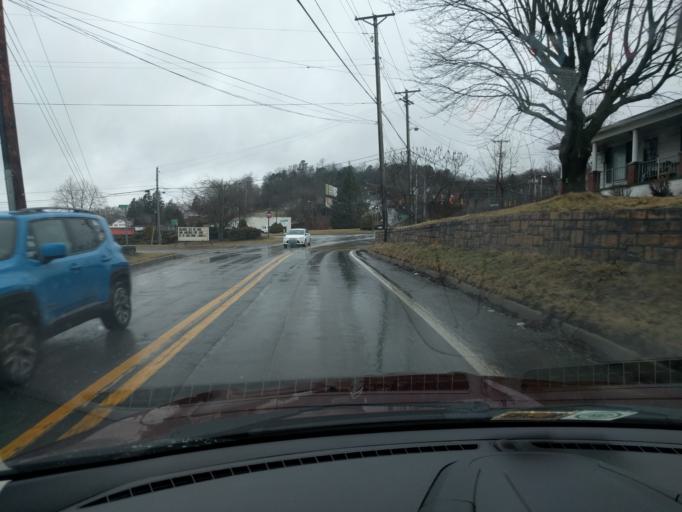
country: US
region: West Virginia
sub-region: Raleigh County
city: Beckley
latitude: 37.7931
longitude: -81.1827
